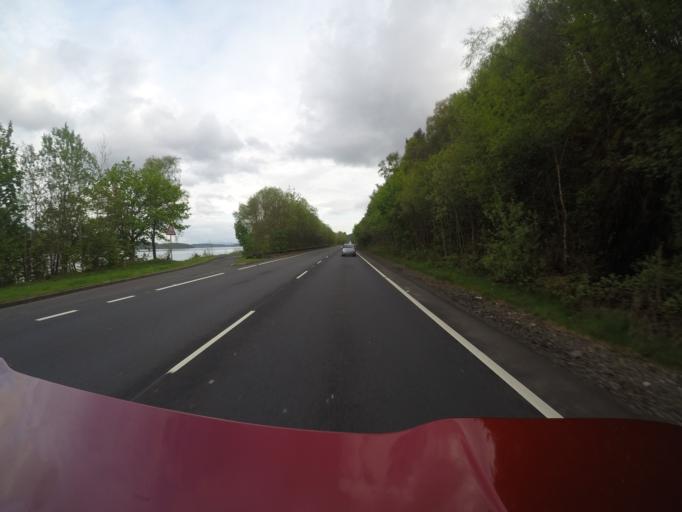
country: GB
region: Scotland
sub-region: Argyll and Bute
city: Helensburgh
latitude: 56.1394
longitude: -4.6608
